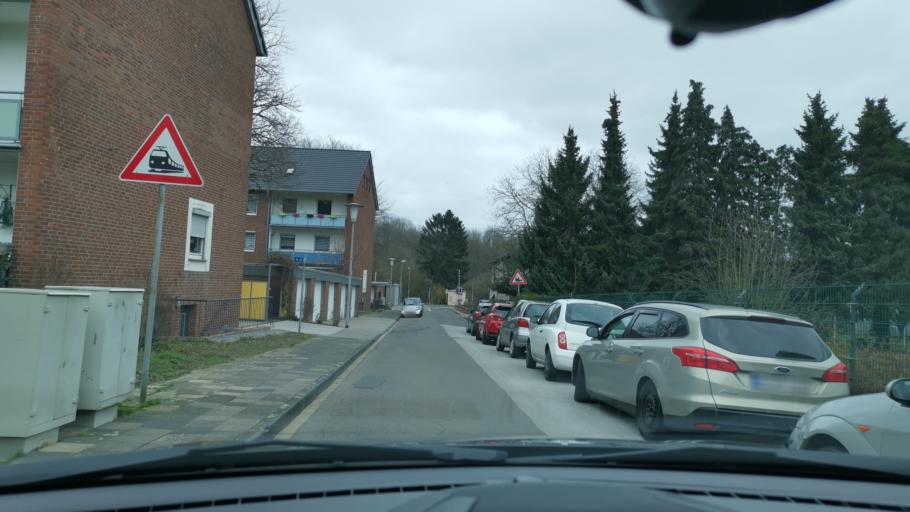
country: DE
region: North Rhine-Westphalia
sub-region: Regierungsbezirk Dusseldorf
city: Grevenbroich
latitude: 51.0761
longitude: 6.5704
